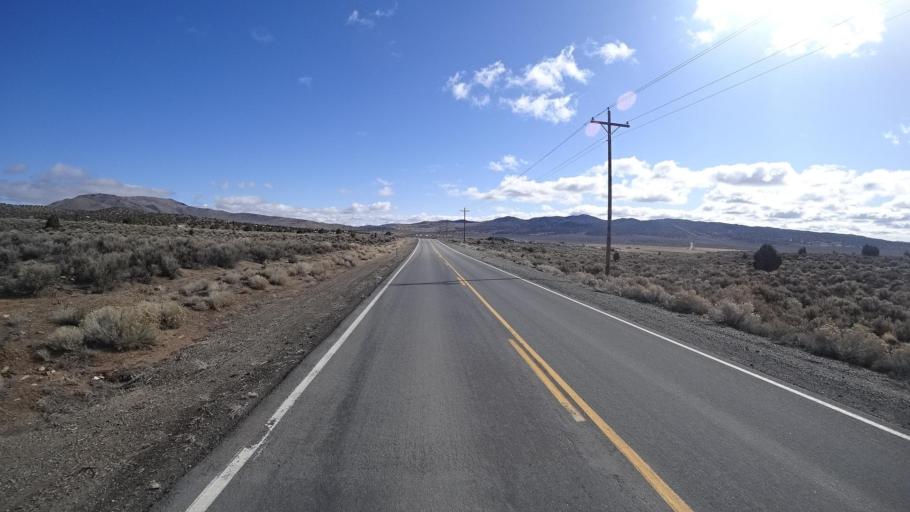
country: US
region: Nevada
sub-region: Washoe County
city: Cold Springs
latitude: 39.7162
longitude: -119.8939
